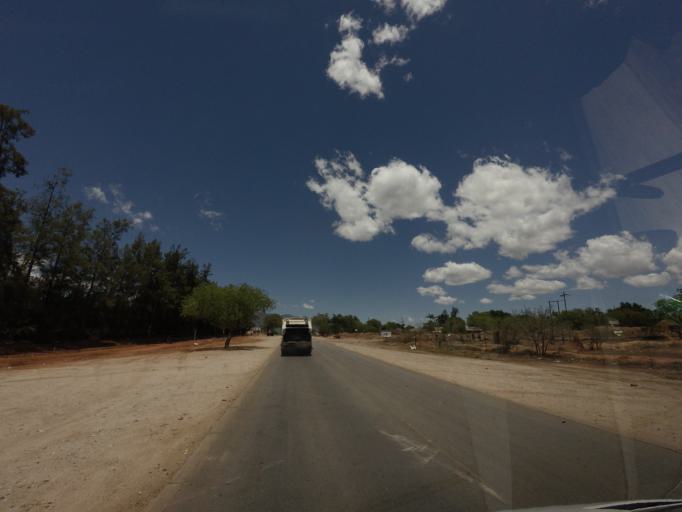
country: ZA
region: Limpopo
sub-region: Mopani District Municipality
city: Hoedspruit
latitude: -24.3859
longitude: 30.8678
